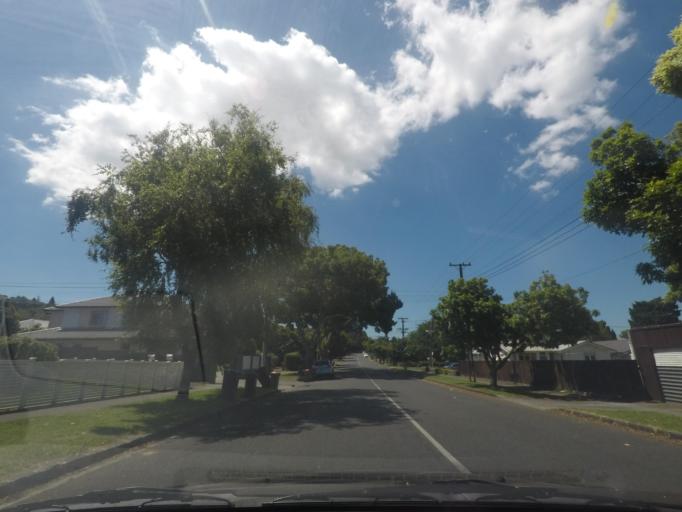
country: NZ
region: Auckland
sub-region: Auckland
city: Auckland
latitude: -36.9056
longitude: 174.7647
